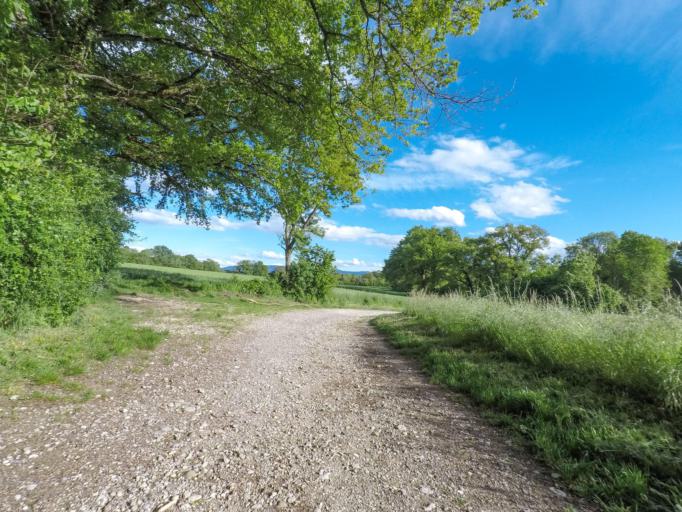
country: FR
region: Rhone-Alpes
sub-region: Departement de l'Ain
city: Chevry
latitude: 46.2698
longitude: 6.0627
